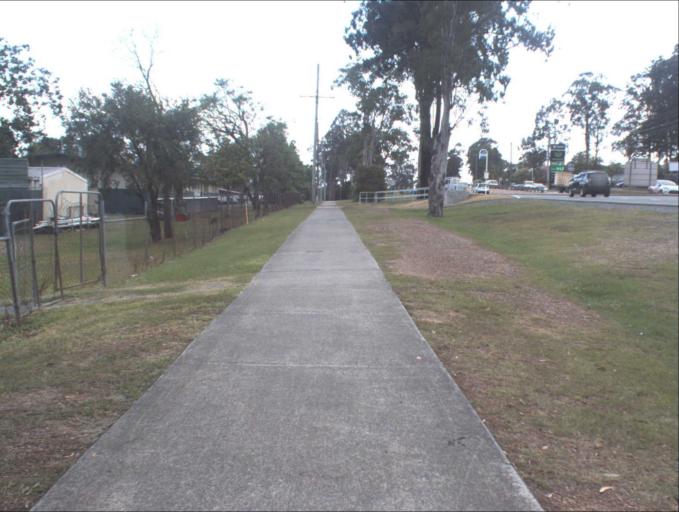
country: AU
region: Queensland
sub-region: Logan
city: Logan City
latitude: -27.6606
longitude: 153.1181
